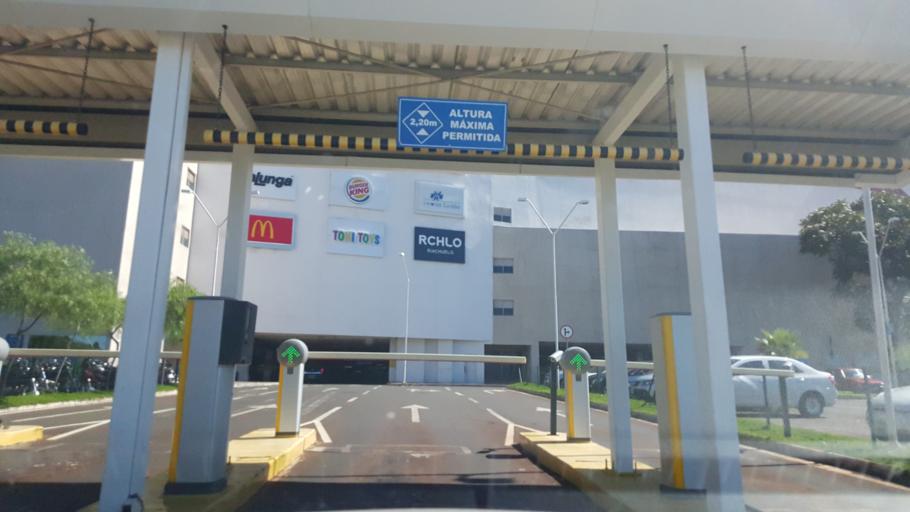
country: AR
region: Misiones
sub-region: Departamento de Iguazu
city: Puerto Iguazu
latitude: -25.5697
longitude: -54.5575
